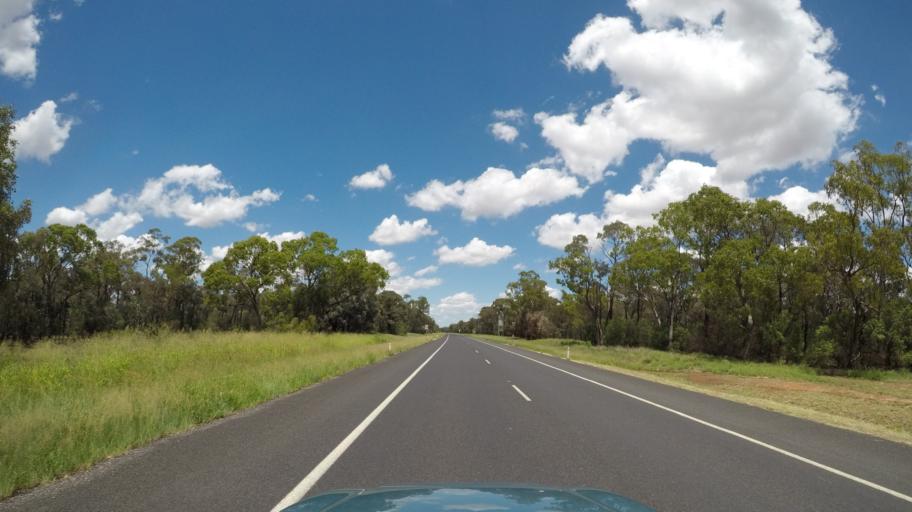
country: AU
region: Queensland
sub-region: Goondiwindi
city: Goondiwindi
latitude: -28.0807
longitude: 150.7396
